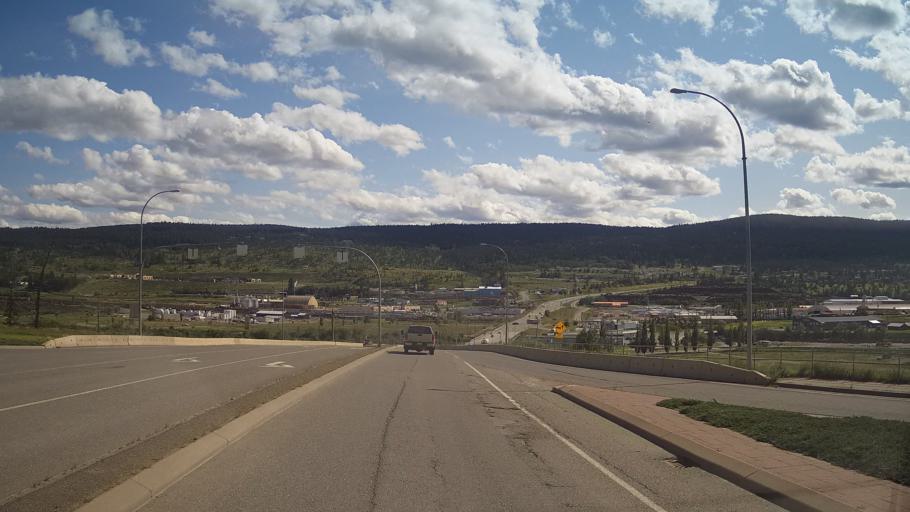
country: CA
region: British Columbia
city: Williams Lake
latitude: 52.1271
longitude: -122.1280
